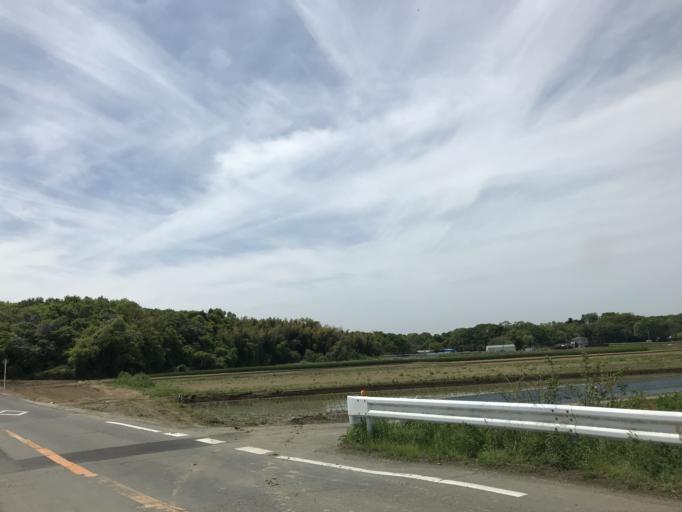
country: JP
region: Ibaraki
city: Mitsukaido
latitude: 35.9969
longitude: 139.9644
